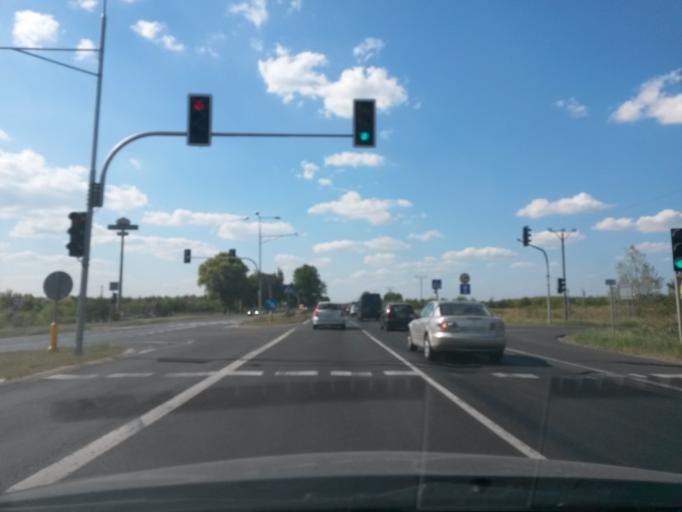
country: PL
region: Masovian Voivodeship
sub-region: Powiat warszawski zachodni
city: Dziekanow Lesny
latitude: 52.3746
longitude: 20.7822
